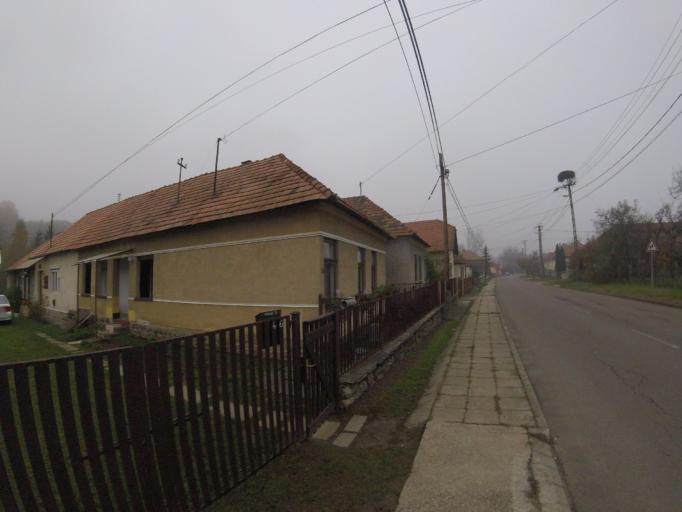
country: HU
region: Heves
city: Szilvasvarad
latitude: 48.1732
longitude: 20.4869
